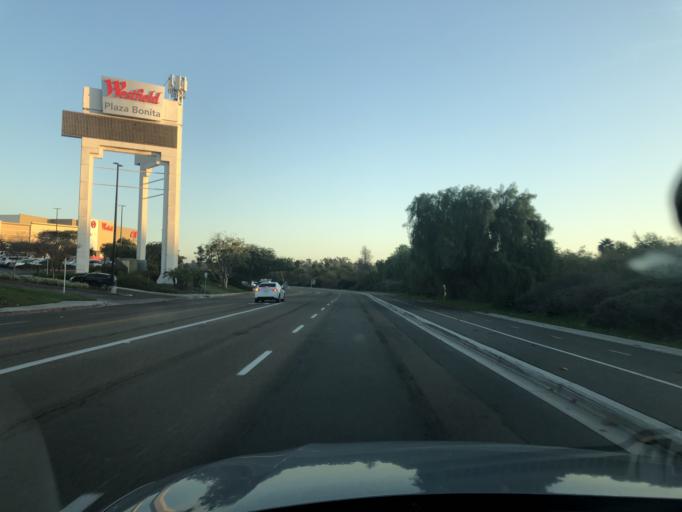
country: US
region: California
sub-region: San Diego County
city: Chula Vista
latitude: 32.6549
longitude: -117.0675
